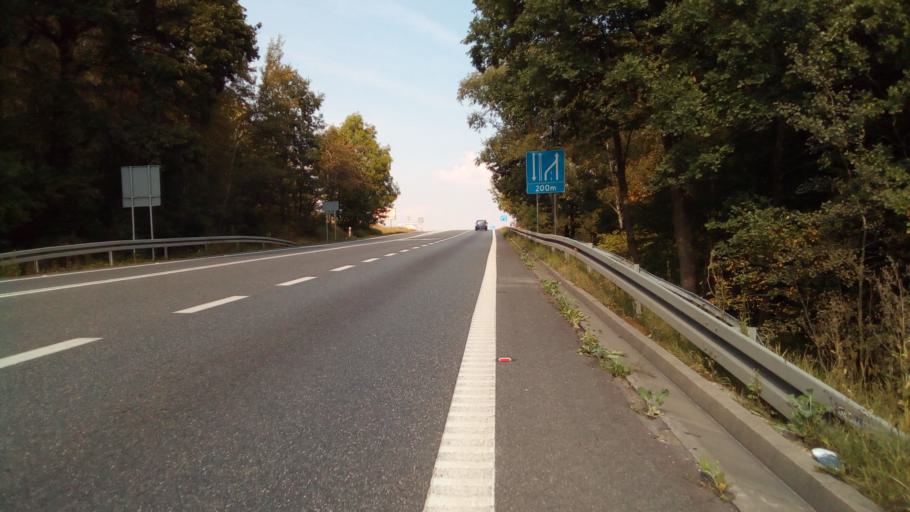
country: PL
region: Subcarpathian Voivodeship
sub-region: Powiat strzyzowski
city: Jawornik
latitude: 49.8351
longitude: 21.8869
